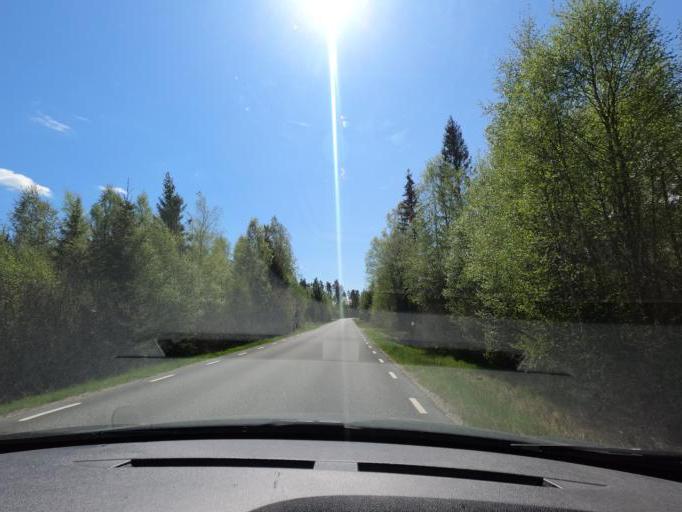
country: SE
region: Joenkoeping
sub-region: Varnamo Kommun
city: Bredaryd
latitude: 57.1582
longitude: 13.7357
